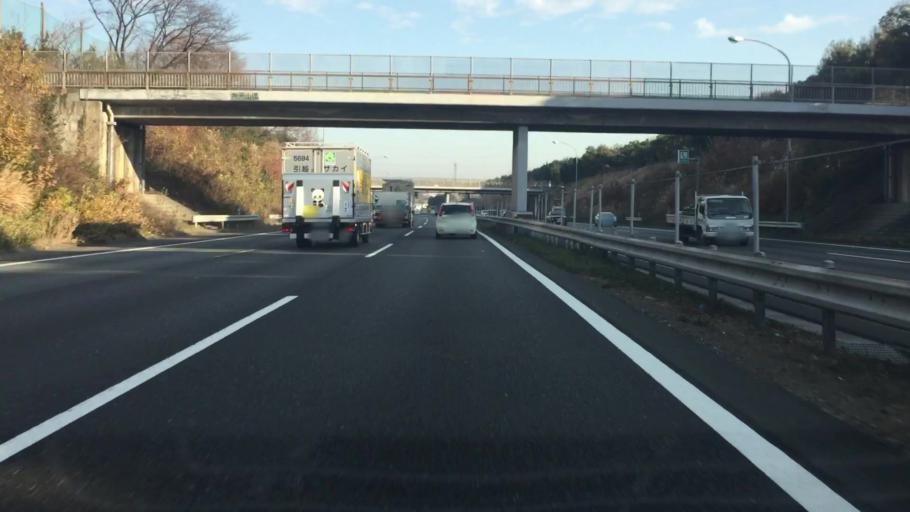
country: JP
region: Saitama
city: Sakado
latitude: 35.9935
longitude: 139.3861
